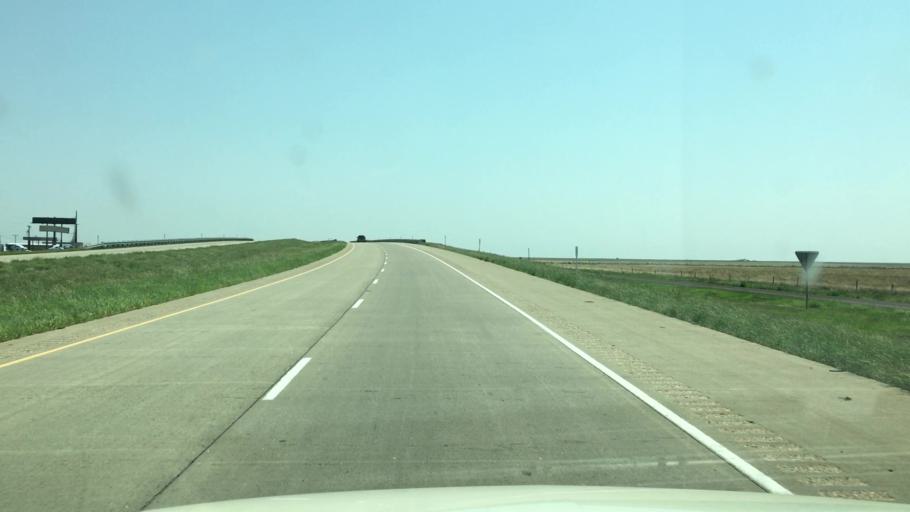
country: US
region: Texas
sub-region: Oldham County
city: Vega
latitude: 35.2691
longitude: -102.5613
